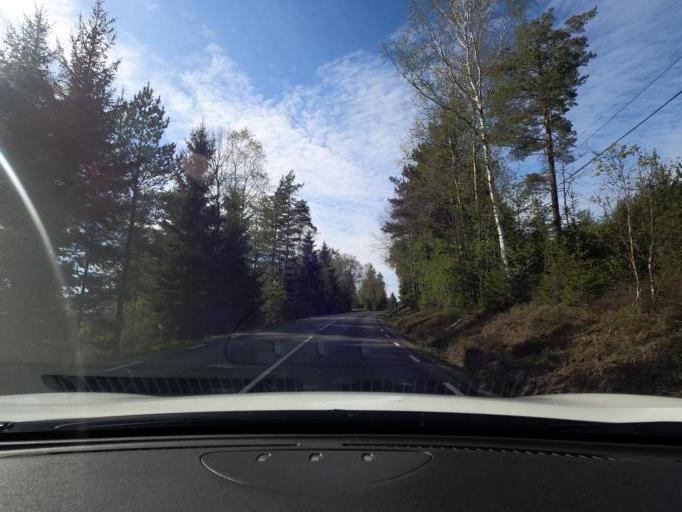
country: SE
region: Vaestra Goetaland
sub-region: Harryda Kommun
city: Landvetter
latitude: 57.6570
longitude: 12.2566
